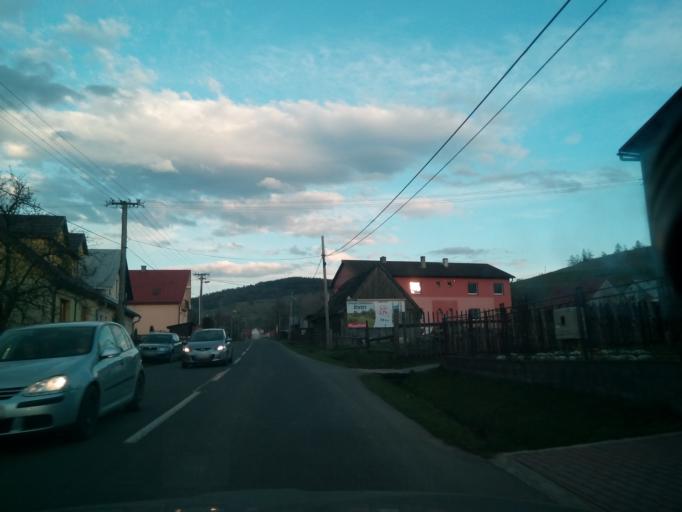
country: SK
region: Presovsky
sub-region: Okres Poprad
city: Zdiar
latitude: 49.3027
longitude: 20.3743
